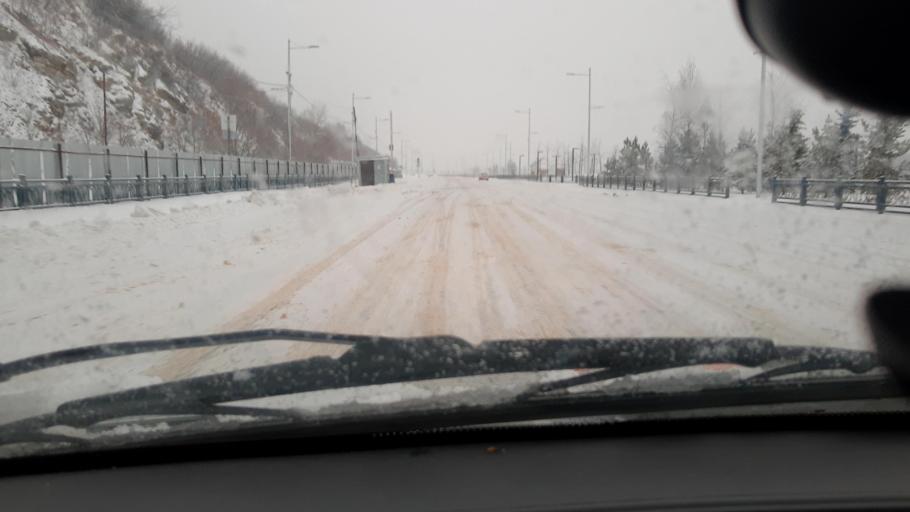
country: RU
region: Bashkortostan
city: Ufa
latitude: 54.7171
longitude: 55.9248
